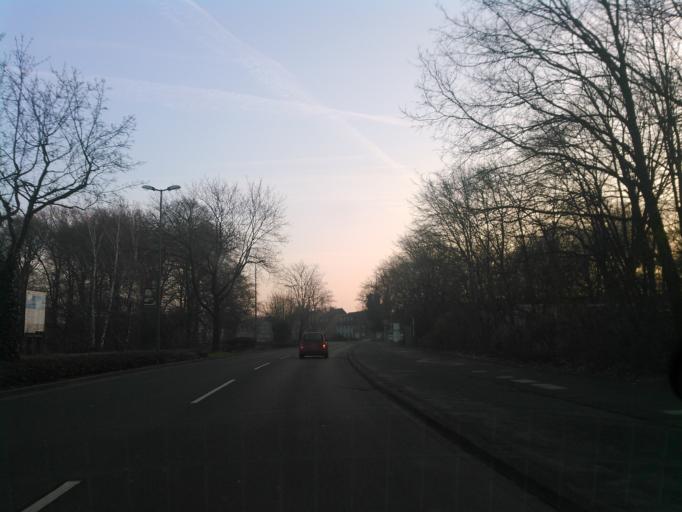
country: DE
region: North Rhine-Westphalia
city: Marl
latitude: 51.6600
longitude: 7.1025
